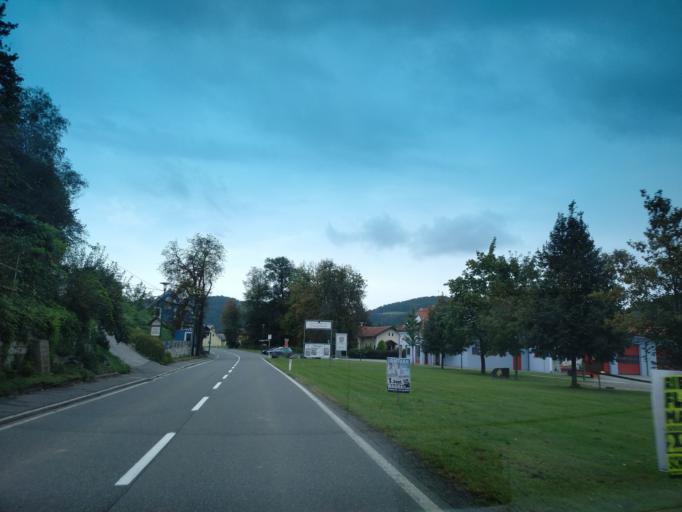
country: AT
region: Styria
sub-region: Politischer Bezirk Leibnitz
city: Kitzeck im Sausal
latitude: 46.7556
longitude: 15.4404
